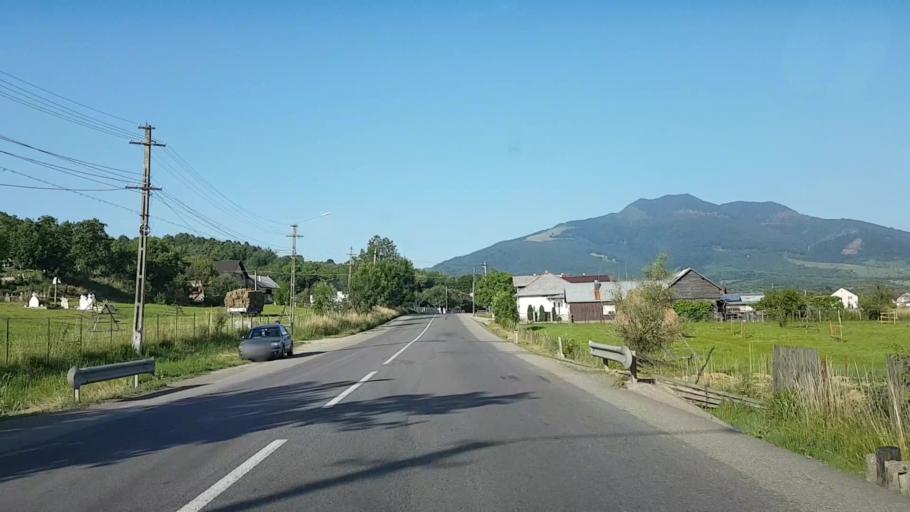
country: RO
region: Bistrita-Nasaud
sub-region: Comuna Tiha Bargaului
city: Tiha Bargaului
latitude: 47.2289
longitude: 24.7758
